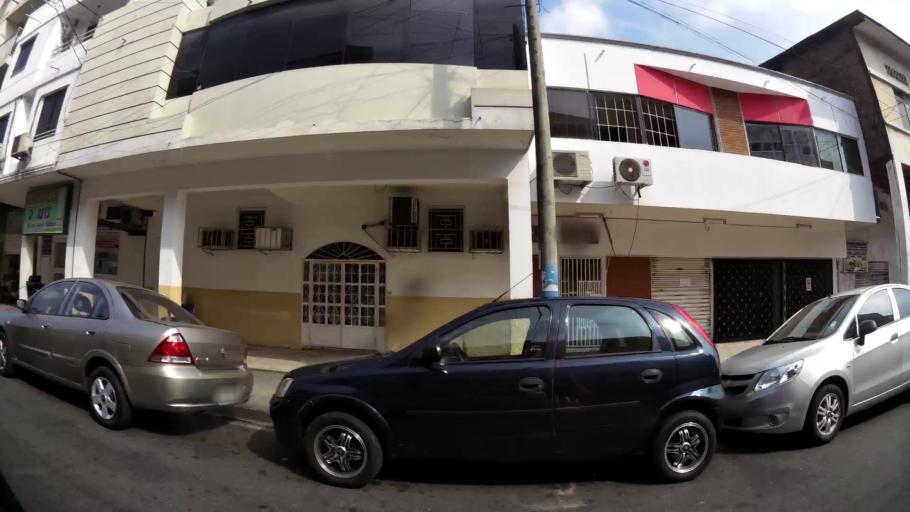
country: EC
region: Guayas
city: Guayaquil
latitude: -2.2042
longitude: -79.9016
